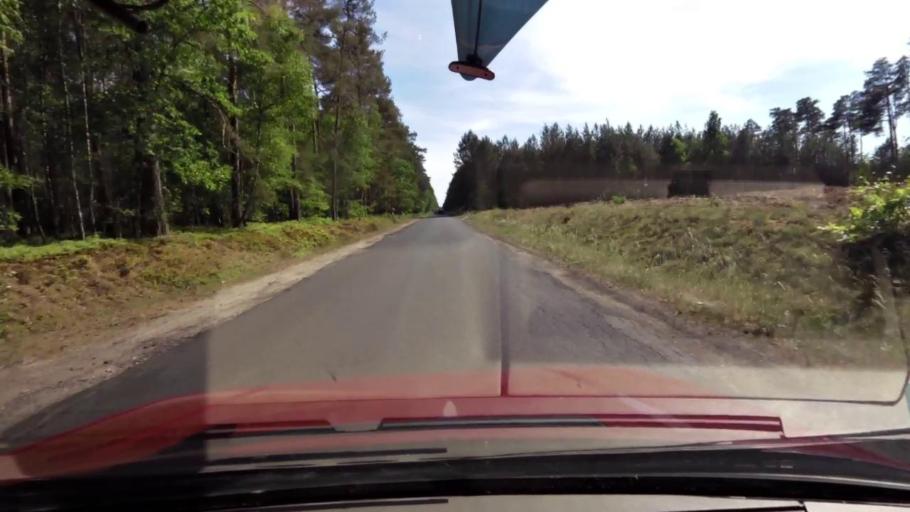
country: PL
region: Pomeranian Voivodeship
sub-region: Powiat slupski
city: Kepice
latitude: 54.3077
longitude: 16.9623
